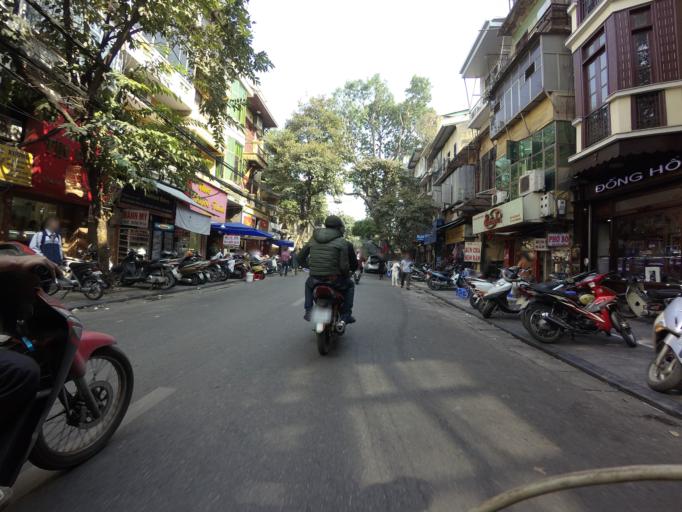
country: VN
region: Ha Noi
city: Hoan Kiem
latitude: 21.0322
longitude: 105.8526
